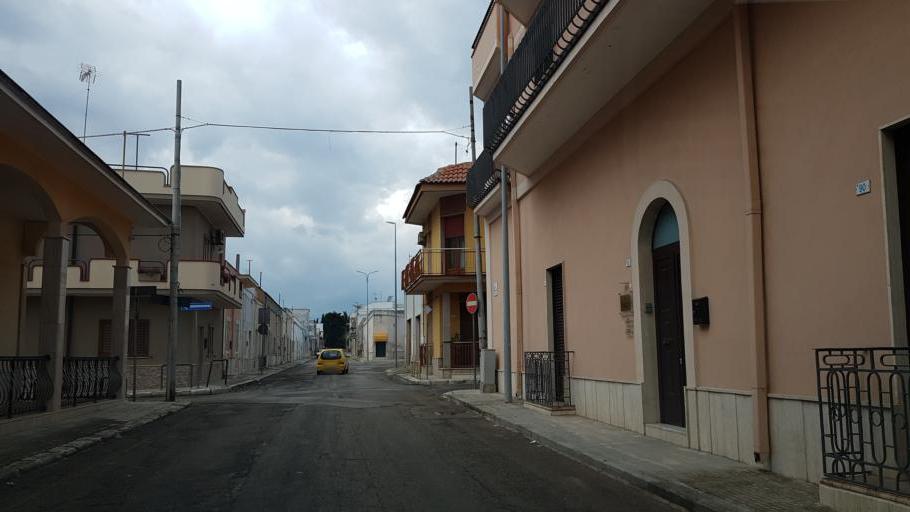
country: IT
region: Apulia
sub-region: Provincia di Brindisi
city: San Donaci
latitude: 40.4489
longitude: 17.9202
